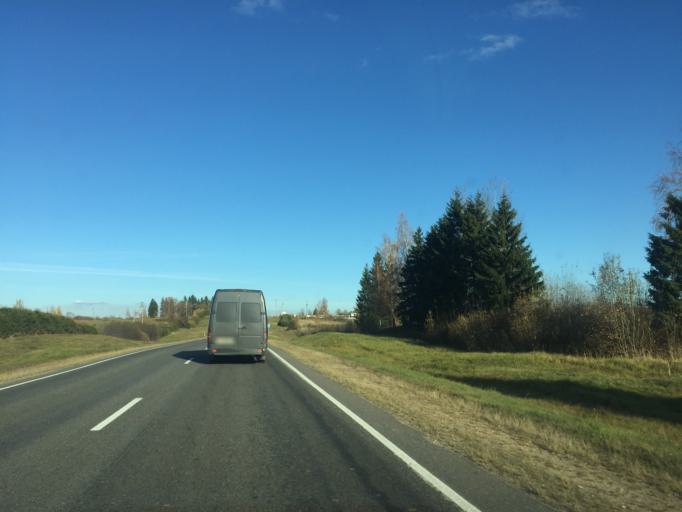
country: BY
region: Vitebsk
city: Dzisna
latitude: 55.2968
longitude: 28.2069
